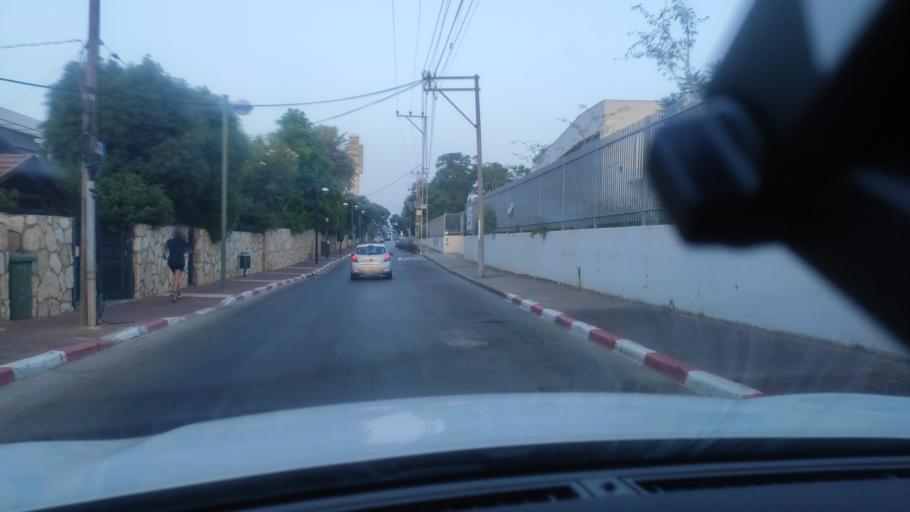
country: IL
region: Central District
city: Kfar Saba
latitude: 32.1849
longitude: 34.9053
